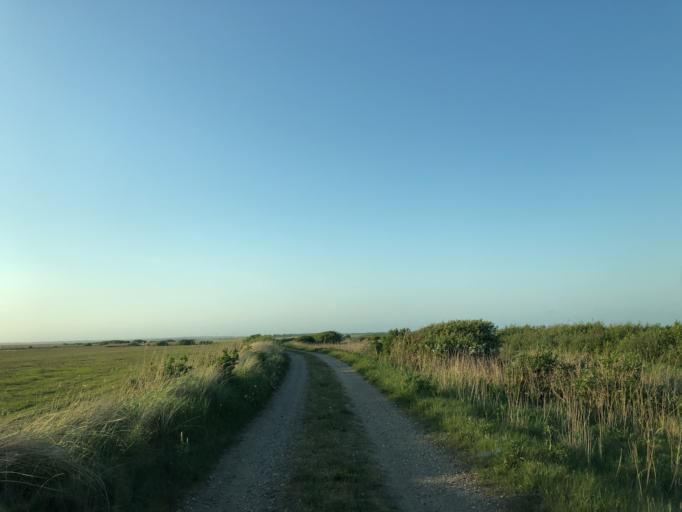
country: DK
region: Central Jutland
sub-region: Ringkobing-Skjern Kommune
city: Ringkobing
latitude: 56.2111
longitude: 8.1631
